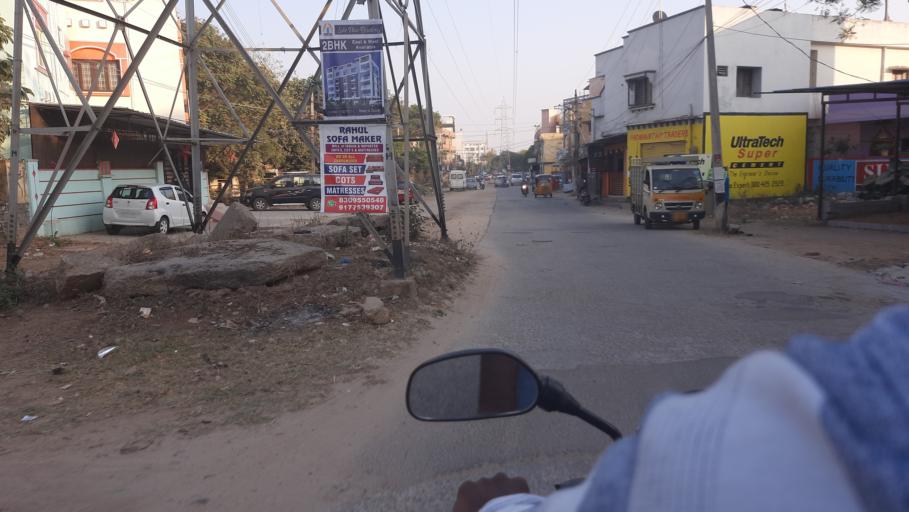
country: IN
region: Telangana
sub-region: Rangareddi
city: Secunderabad
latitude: 17.4983
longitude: 78.5416
